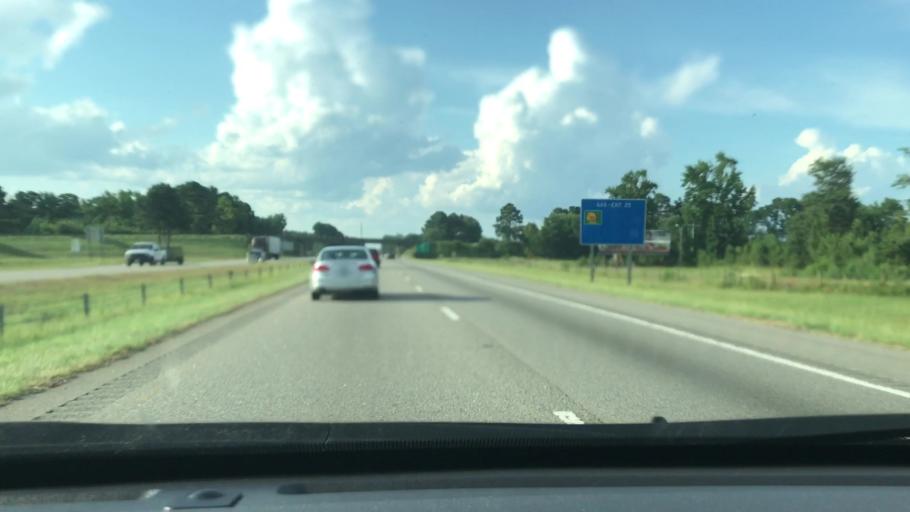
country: US
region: North Carolina
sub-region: Robeson County
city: Saint Pauls
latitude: 34.7175
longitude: -78.9973
